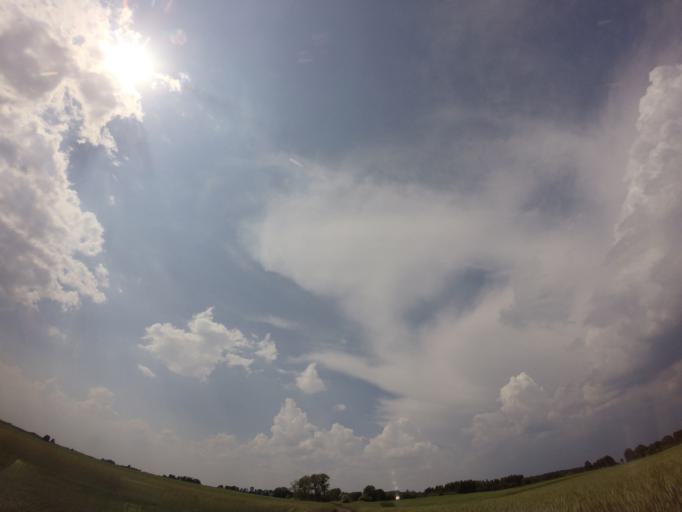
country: PL
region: West Pomeranian Voivodeship
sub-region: Powiat choszczenski
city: Bierzwnik
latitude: 53.1164
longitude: 15.6043
